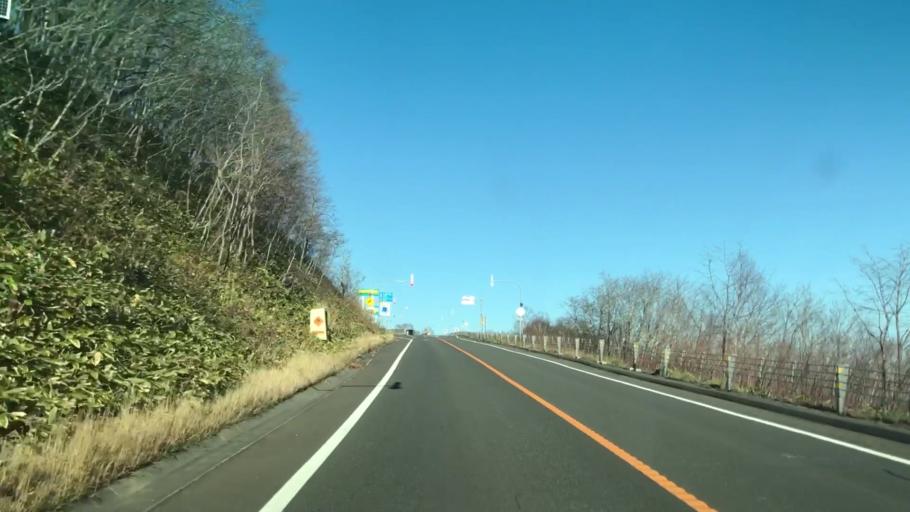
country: JP
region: Hokkaido
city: Otofuke
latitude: 42.9673
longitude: 142.7963
